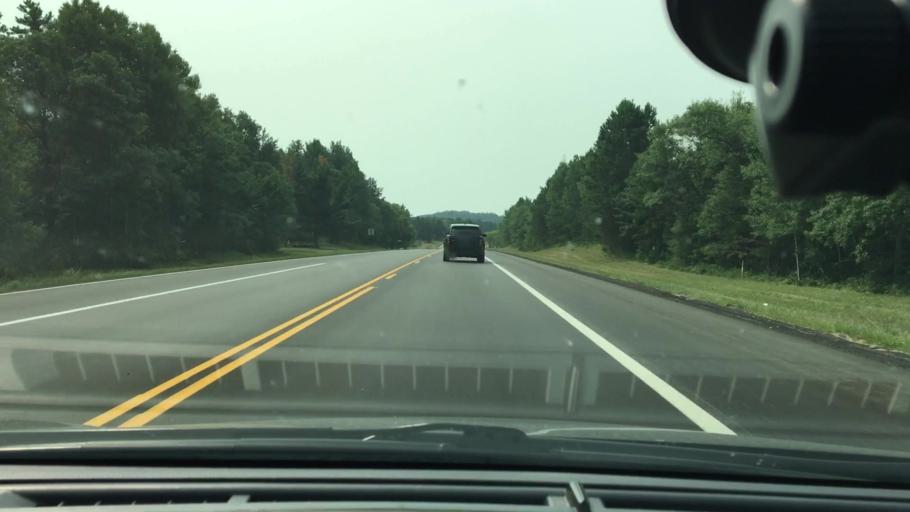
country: US
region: Minnesota
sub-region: Crow Wing County
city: Brainerd
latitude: 46.4093
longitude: -94.1760
